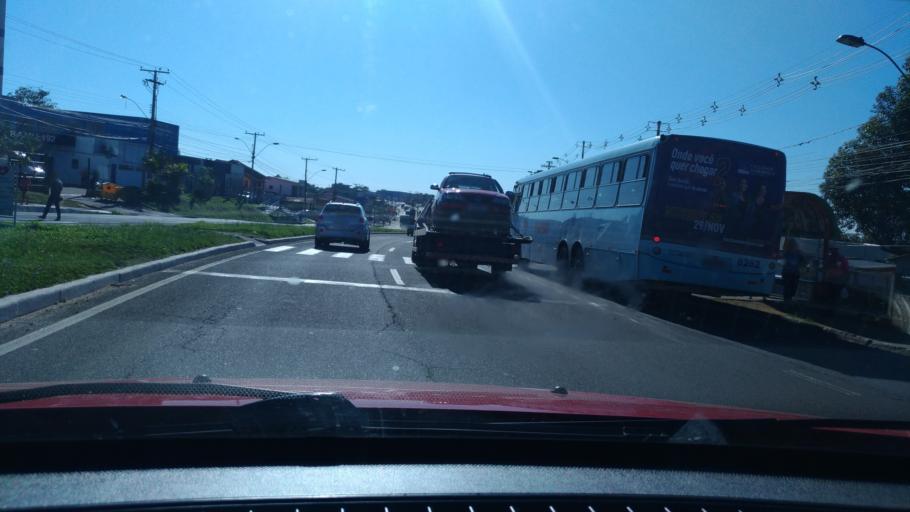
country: BR
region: Rio Grande do Sul
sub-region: Viamao
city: Viamao
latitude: -30.0928
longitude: -51.0709
